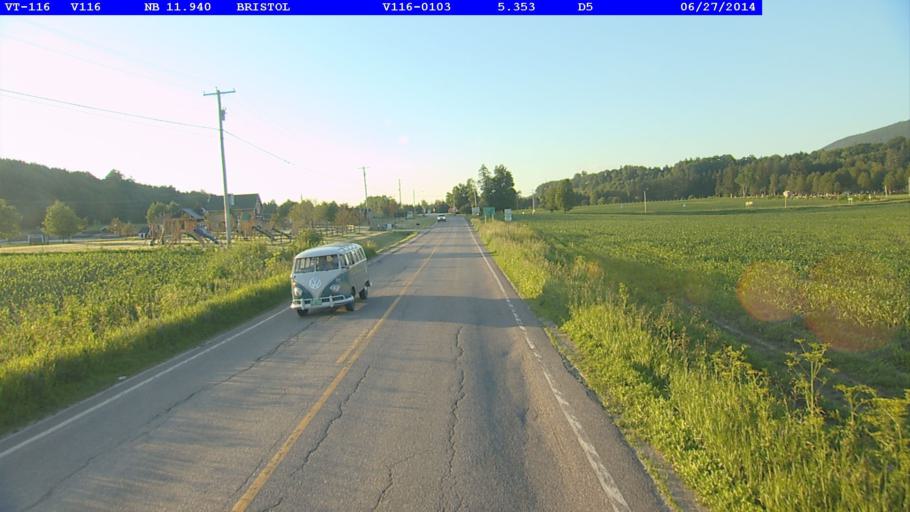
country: US
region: Vermont
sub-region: Addison County
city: Bristol
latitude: 44.1275
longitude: -73.0974
